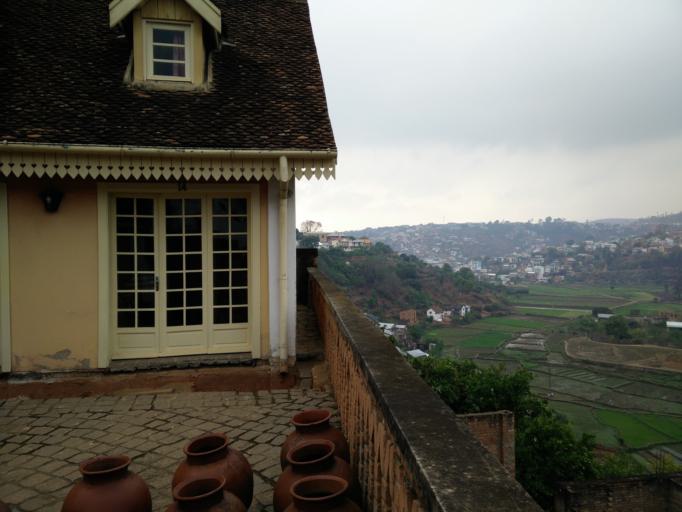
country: MG
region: Upper Matsiatra
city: Fianarantsoa
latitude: -21.4557
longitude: 47.0803
